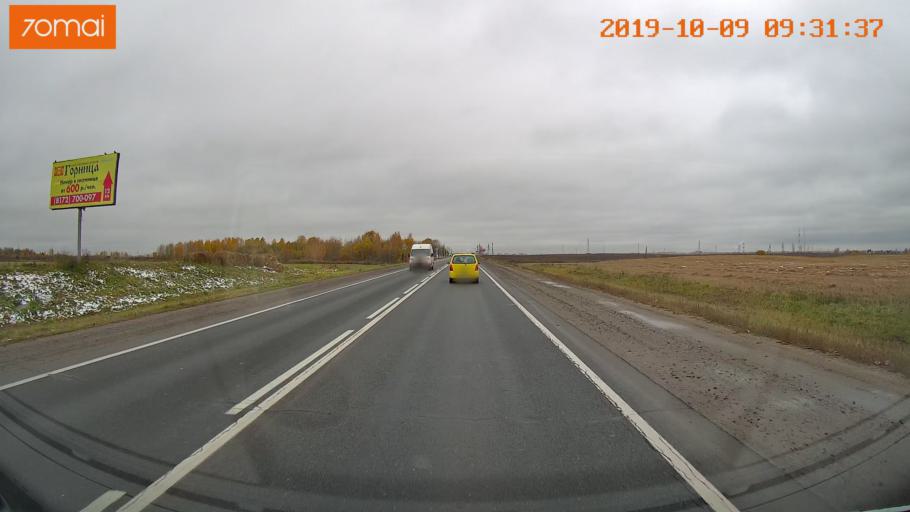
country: RU
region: Vologda
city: Vologda
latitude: 59.1509
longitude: 39.9371
